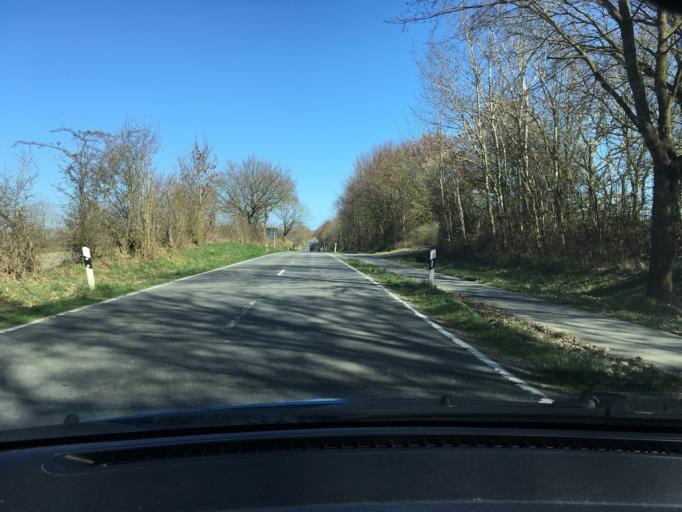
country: DE
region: Schleswig-Holstein
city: Kosel
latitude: 54.4929
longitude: 9.7476
